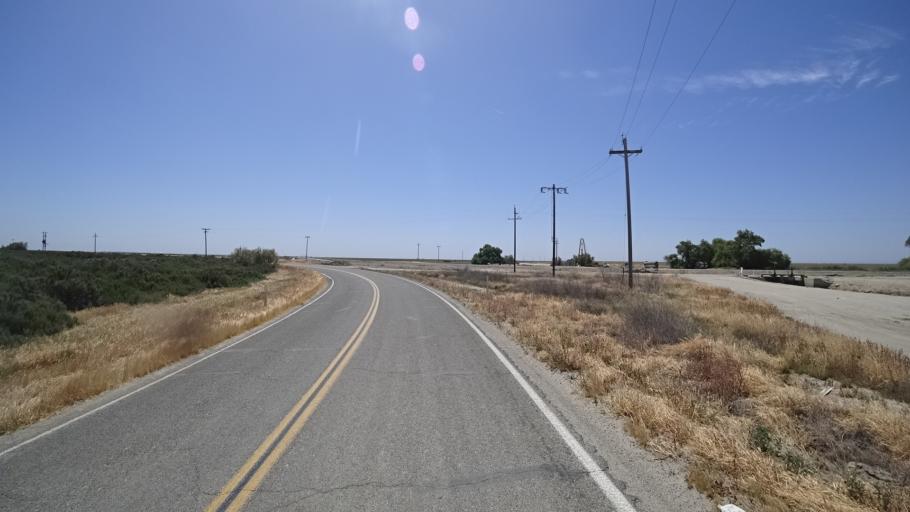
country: US
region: California
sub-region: Kings County
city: Stratford
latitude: 36.1386
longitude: -119.7171
